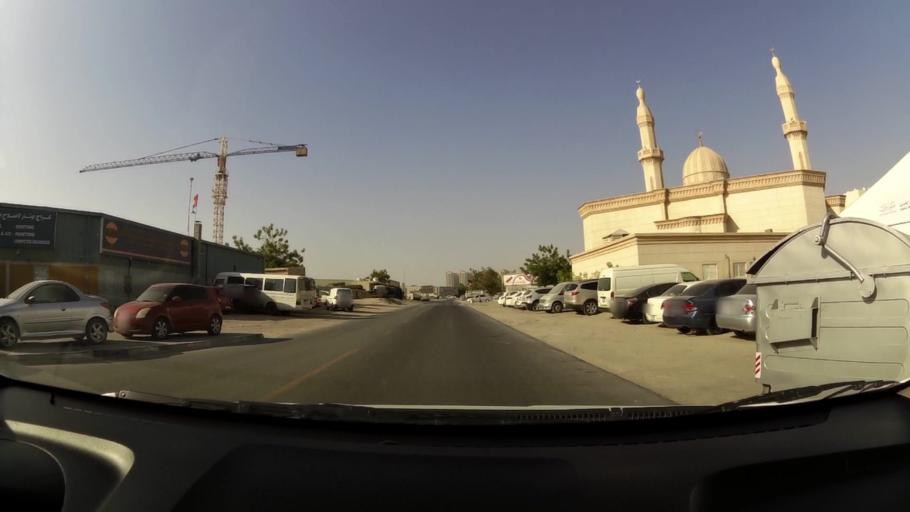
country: AE
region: Ash Shariqah
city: Sharjah
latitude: 25.2844
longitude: 55.3871
